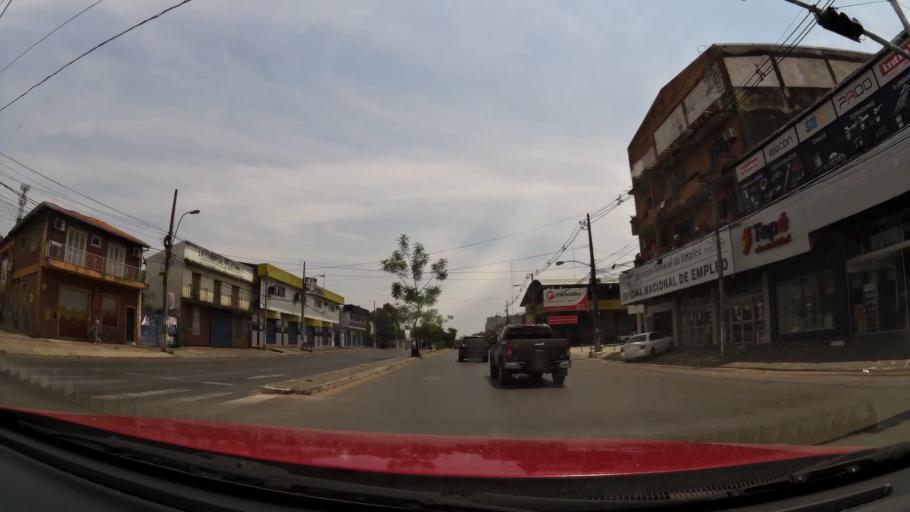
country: PY
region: Central
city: Lambare
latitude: -25.3107
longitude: -57.5904
